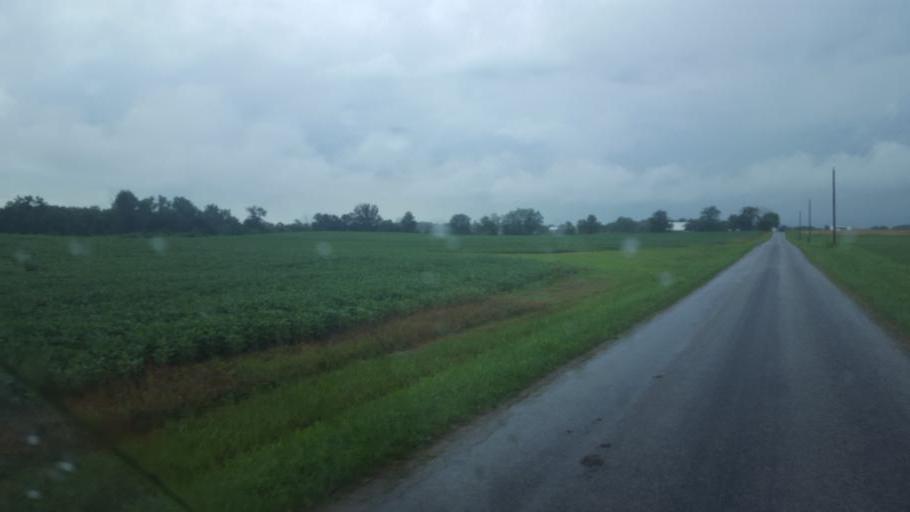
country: US
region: Ohio
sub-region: Union County
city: Richwood
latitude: 40.5585
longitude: -83.4055
